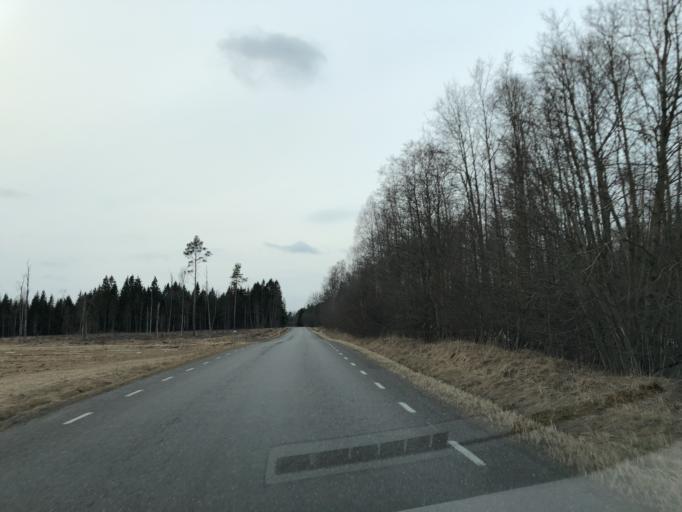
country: EE
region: Paernumaa
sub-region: Vaendra vald (alev)
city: Vandra
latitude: 58.6861
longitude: 24.9892
